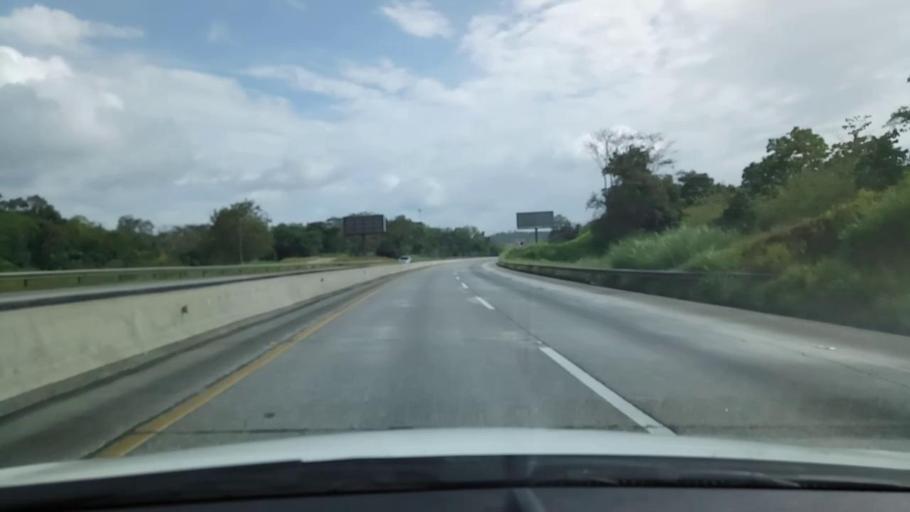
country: PA
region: Colon
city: El Giral
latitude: 9.2582
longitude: -79.6937
